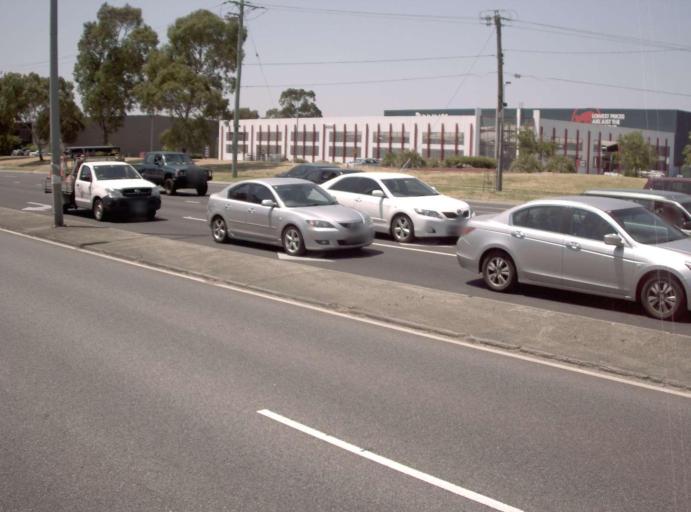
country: AU
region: Victoria
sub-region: Kingston
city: Dingley Village
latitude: -37.9905
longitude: 145.1446
